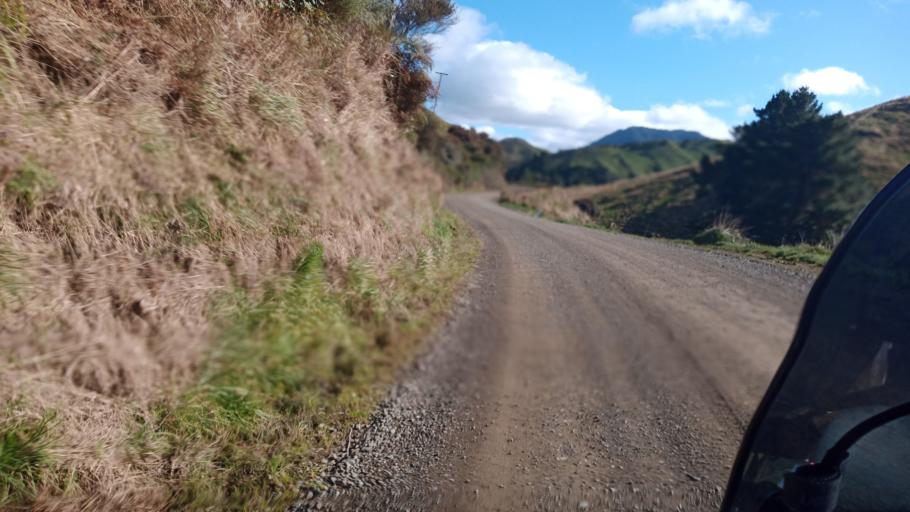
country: NZ
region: Bay of Plenty
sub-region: Opotiki District
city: Opotiki
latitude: -38.4684
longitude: 177.4295
